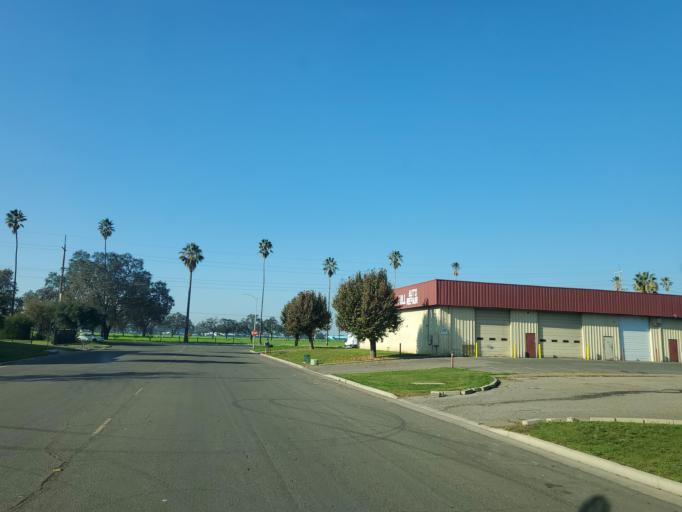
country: US
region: California
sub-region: San Joaquin County
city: August
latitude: 37.9862
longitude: -121.2568
